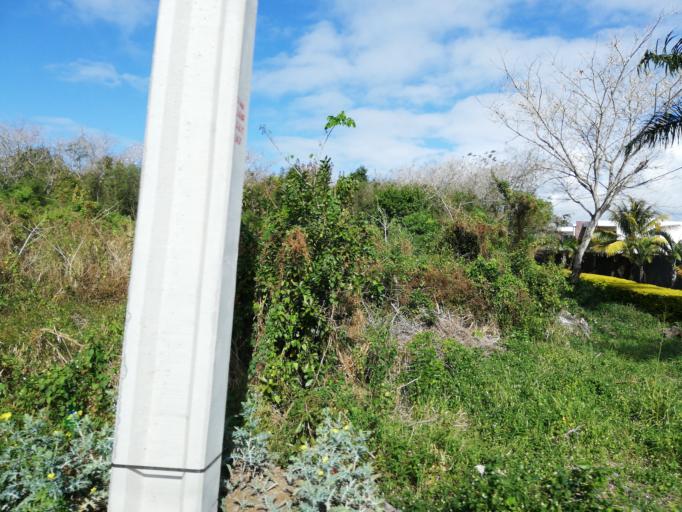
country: MU
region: Riviere du Rempart
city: Petit Raffray
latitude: -20.0080
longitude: 57.5980
